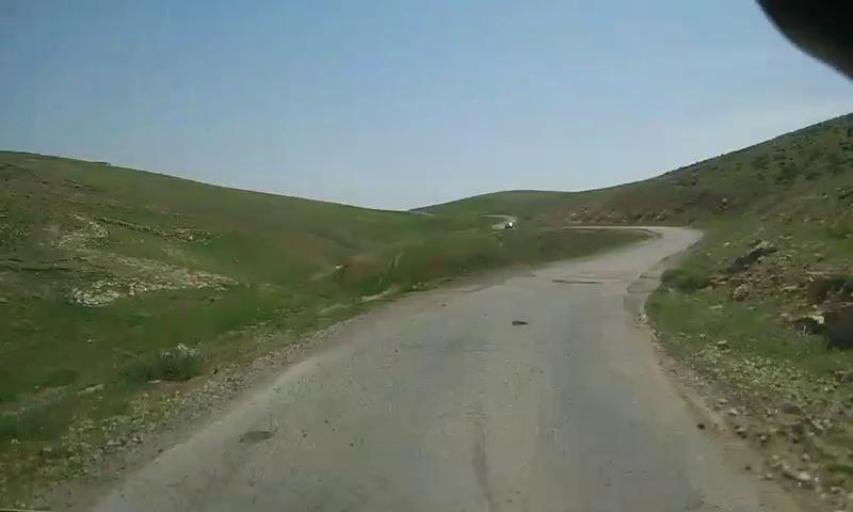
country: PS
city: `Arab ar Rashaydah
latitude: 31.5553
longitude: 35.2491
